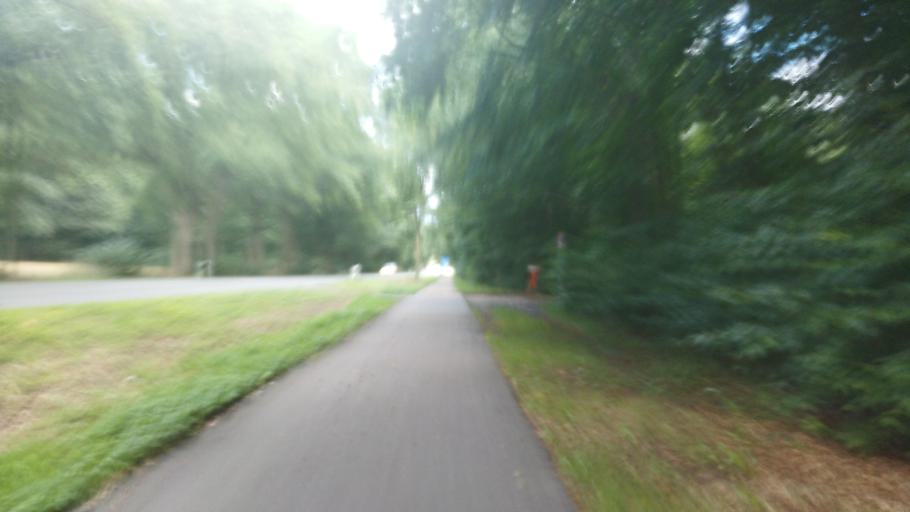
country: DE
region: North Rhine-Westphalia
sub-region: Regierungsbezirk Munster
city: Haltern
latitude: 51.7178
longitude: 7.1899
